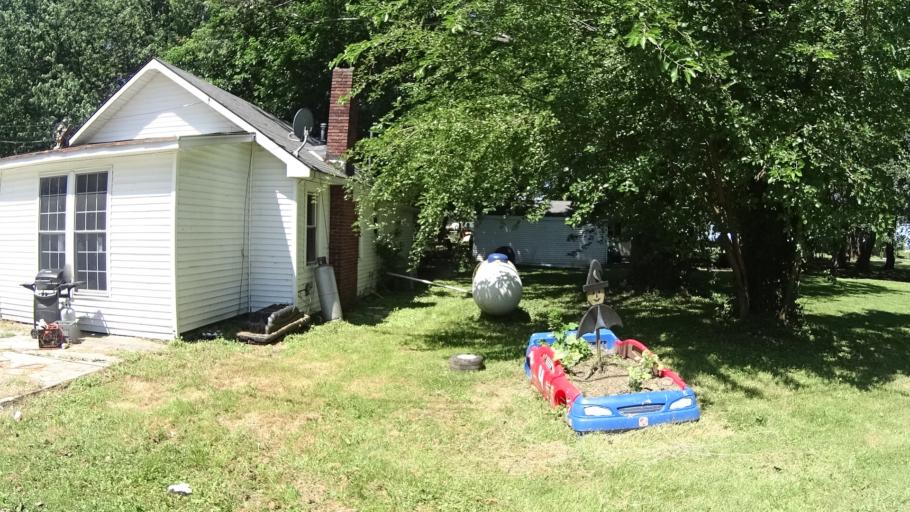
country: US
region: Ohio
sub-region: Ottawa County
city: Port Clinton
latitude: 41.4489
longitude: -82.8398
